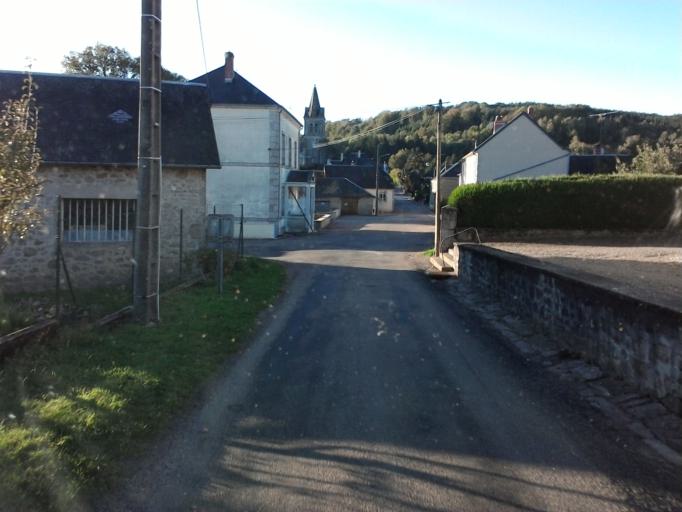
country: FR
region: Bourgogne
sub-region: Departement de la Nievre
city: Lormes
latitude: 47.2864
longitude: 4.0155
